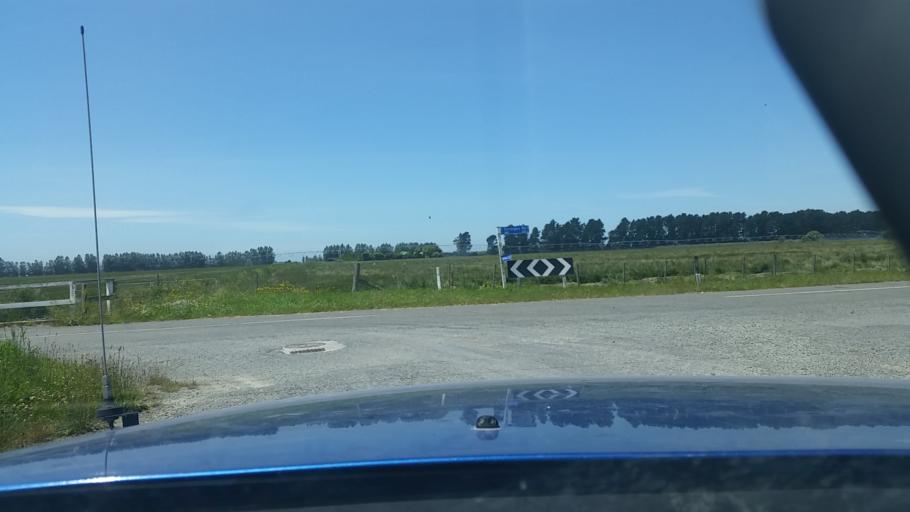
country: NZ
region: Canterbury
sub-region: Ashburton District
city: Tinwald
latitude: -43.9734
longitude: 171.7531
